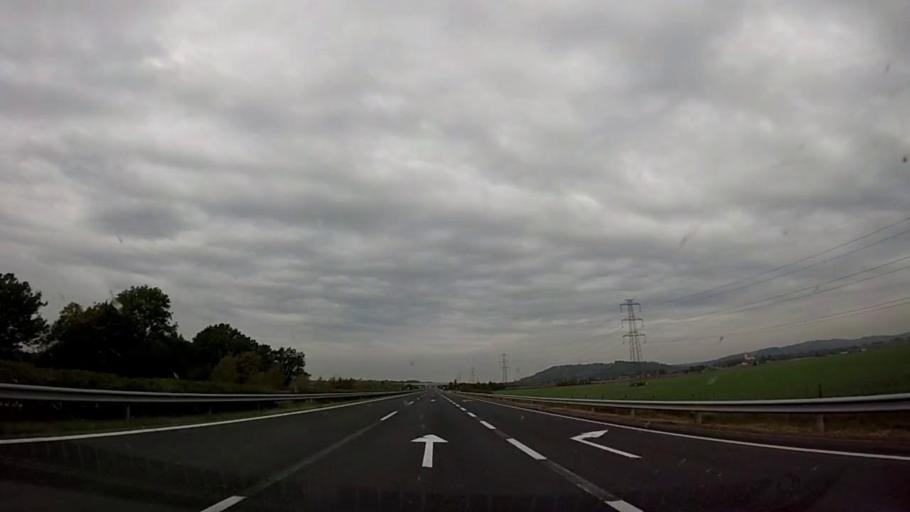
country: HR
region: Medimurska
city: Podturen
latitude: 46.5089
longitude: 16.5678
